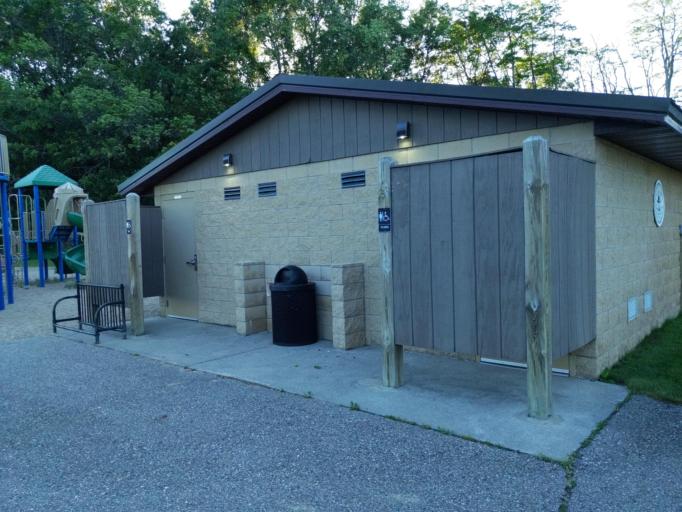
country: US
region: Michigan
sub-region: Muskegon County
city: Whitehall
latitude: 43.4022
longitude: -86.3591
